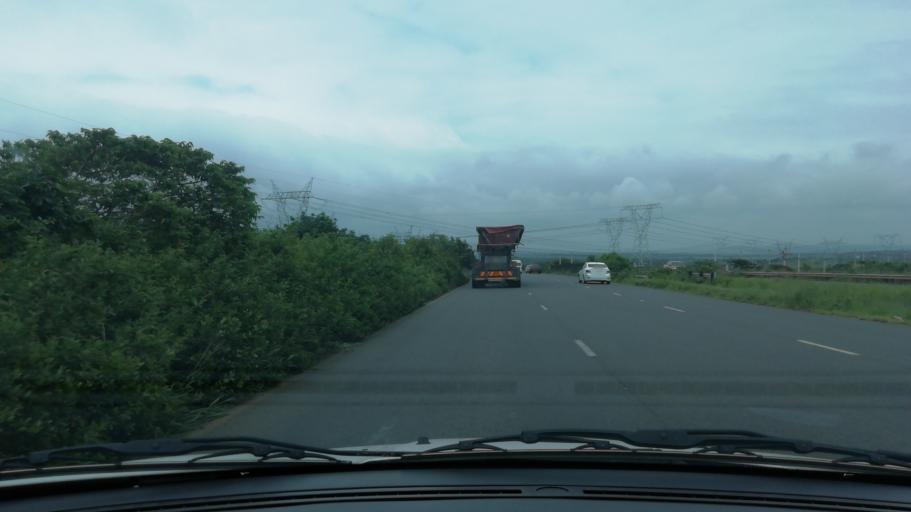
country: ZA
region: KwaZulu-Natal
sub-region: uThungulu District Municipality
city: Richards Bay
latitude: -28.7765
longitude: 32.0062
